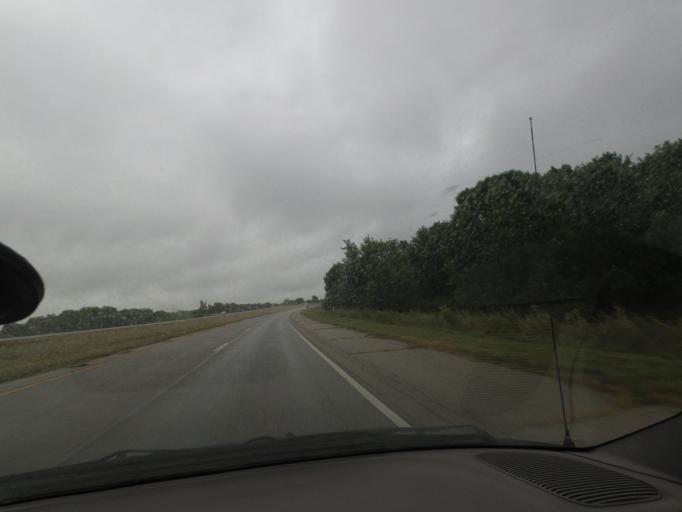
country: US
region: Illinois
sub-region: Pike County
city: Barry
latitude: 39.7374
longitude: -91.1276
